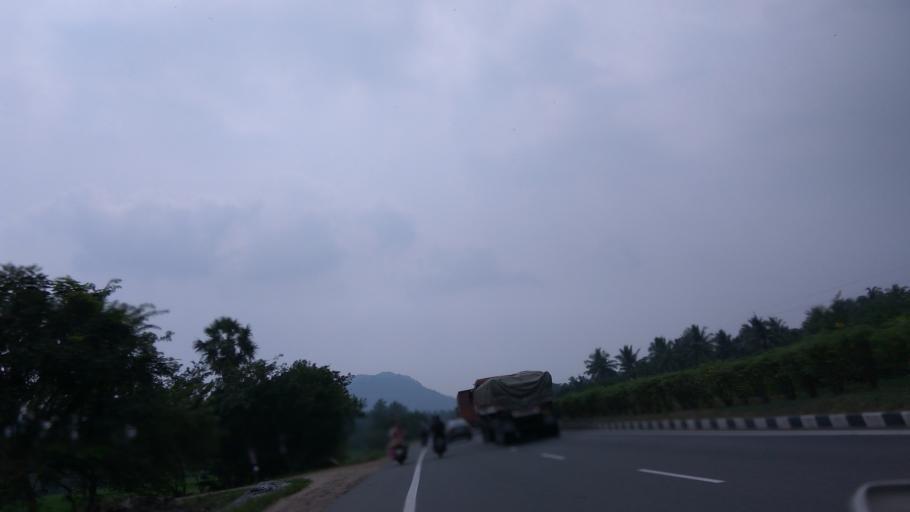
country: IN
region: Tamil Nadu
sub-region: Krishnagiri
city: Kaverippattanam
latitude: 12.3940
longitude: 78.2186
